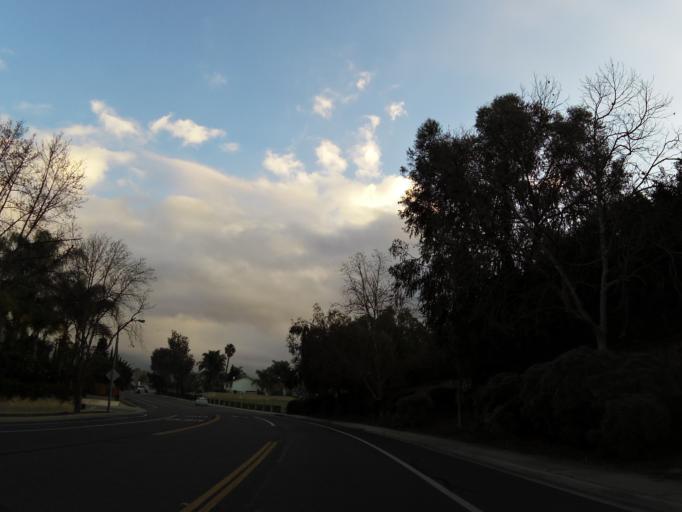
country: US
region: California
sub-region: Ventura County
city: Casa Conejo
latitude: 34.1630
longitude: -118.9443
